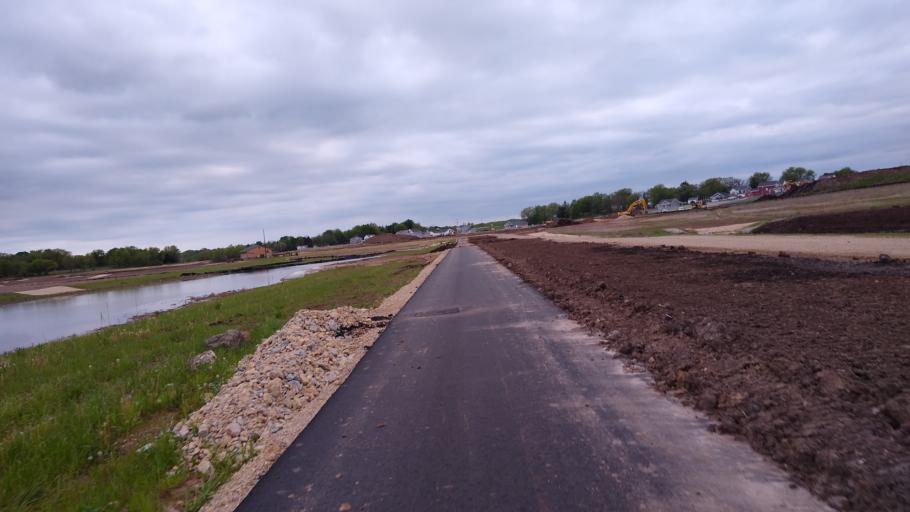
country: US
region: Wisconsin
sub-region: Dane County
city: Monona
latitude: 43.0120
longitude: -89.3677
